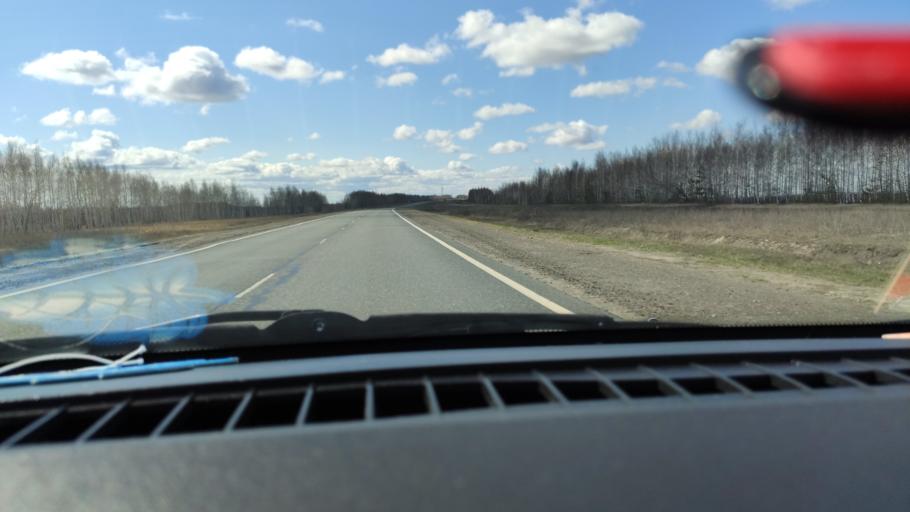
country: RU
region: Saratov
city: Dukhovnitskoye
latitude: 52.8472
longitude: 48.2537
